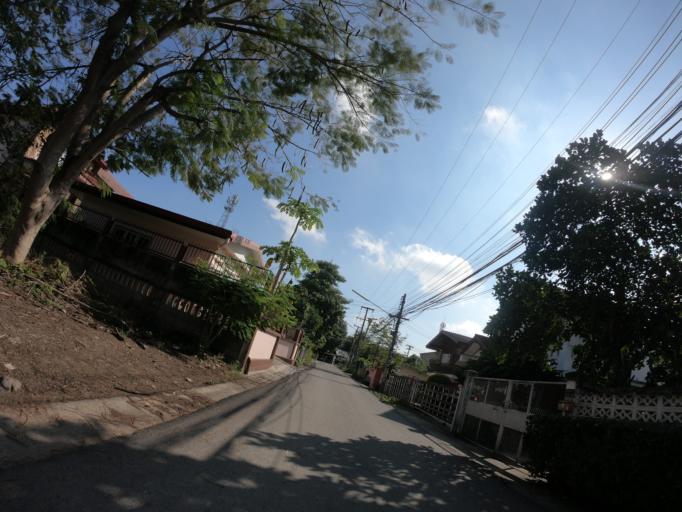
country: TH
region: Chiang Mai
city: Chiang Mai
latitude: 18.7835
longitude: 99.0376
